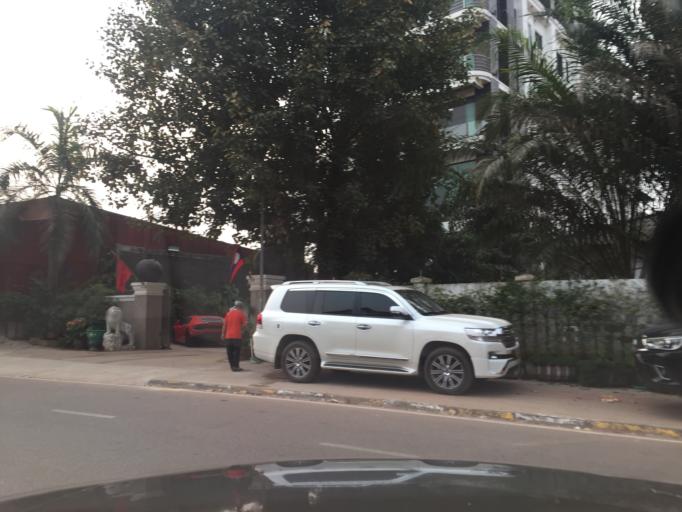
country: LA
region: Vientiane
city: Vientiane
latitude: 17.9730
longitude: 102.6034
